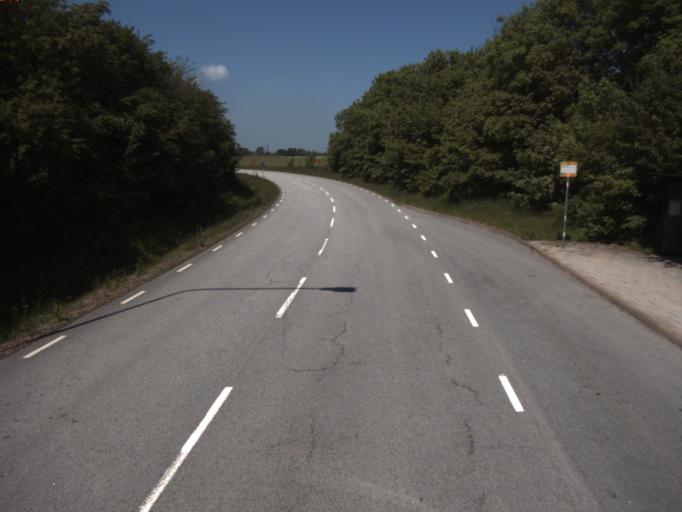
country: SE
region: Skane
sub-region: Helsingborg
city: Barslov
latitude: 56.0062
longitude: 12.8148
